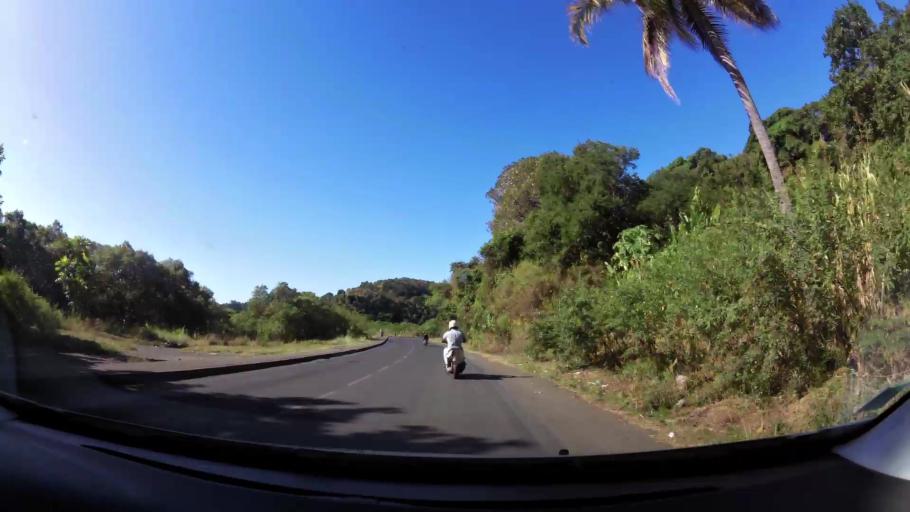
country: YT
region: Mamoudzou
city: Mamoudzou
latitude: -12.7754
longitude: 45.2283
